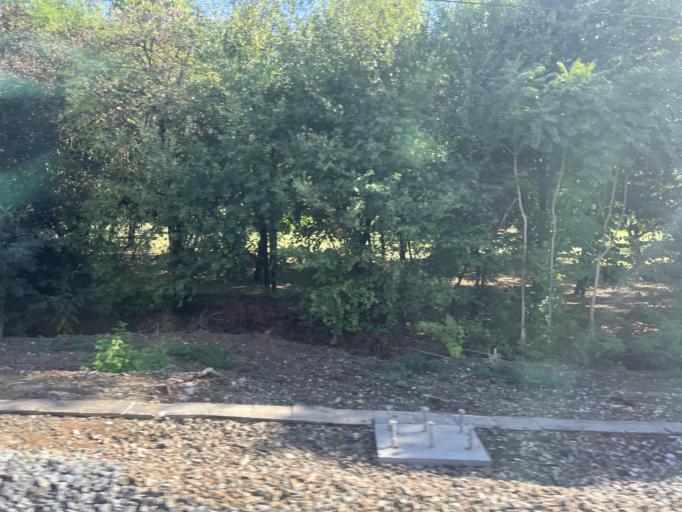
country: IT
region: Emilia-Romagna
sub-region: Provincia di Parma
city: Parma
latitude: 44.8149
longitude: 10.2924
